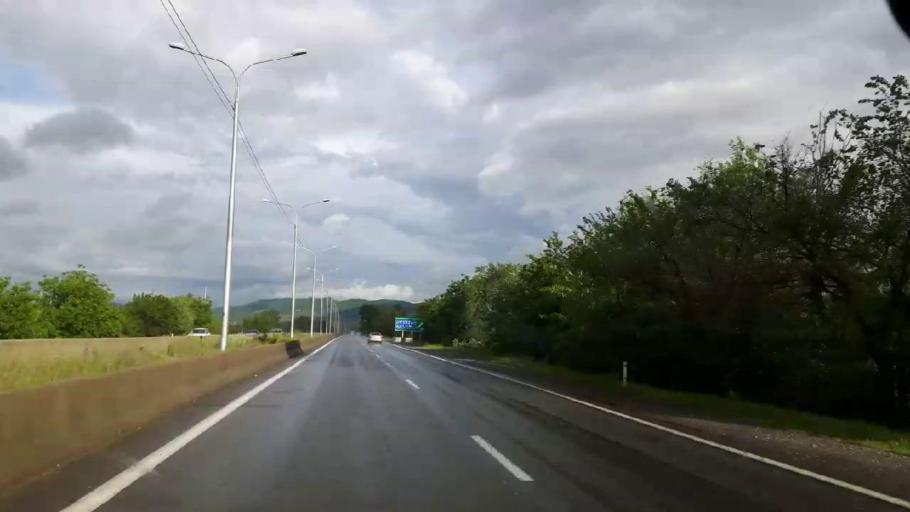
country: GE
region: Shida Kartli
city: Kaspi
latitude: 41.9206
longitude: 44.5481
